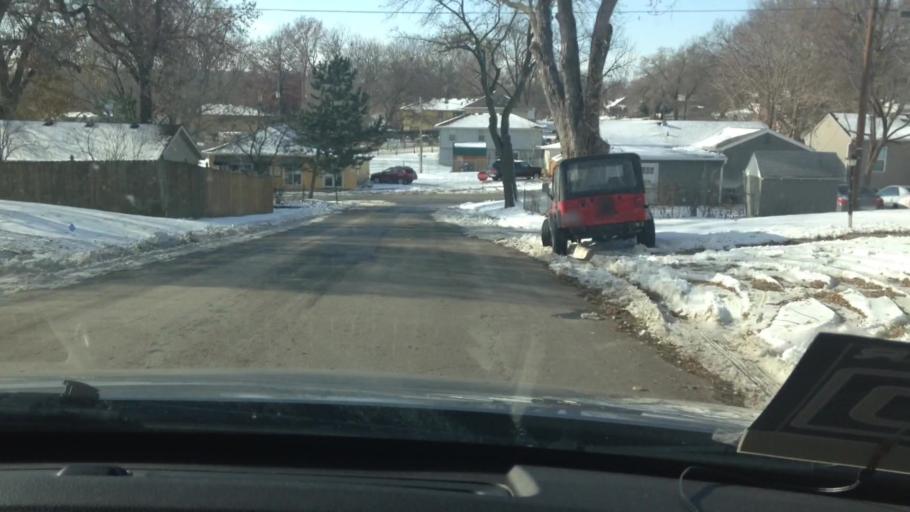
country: US
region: Kansas
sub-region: Leavenworth County
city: Leavenworth
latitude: 39.3004
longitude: -94.9128
